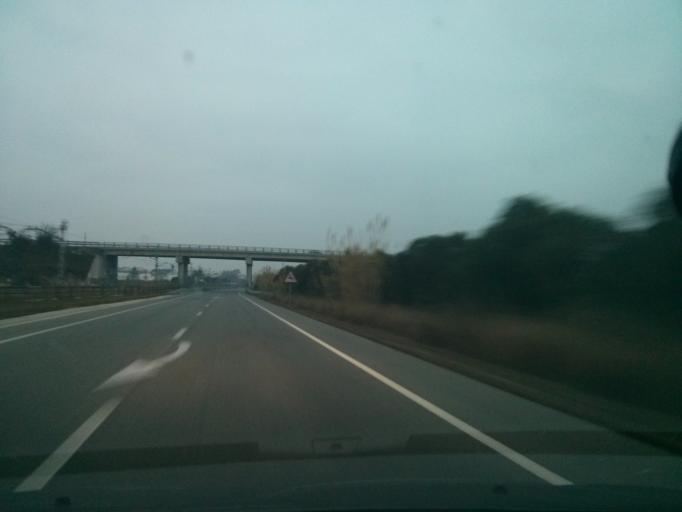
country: ES
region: Catalonia
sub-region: Provincia de Tarragona
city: El Vendrell
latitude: 41.2063
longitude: 1.5343
